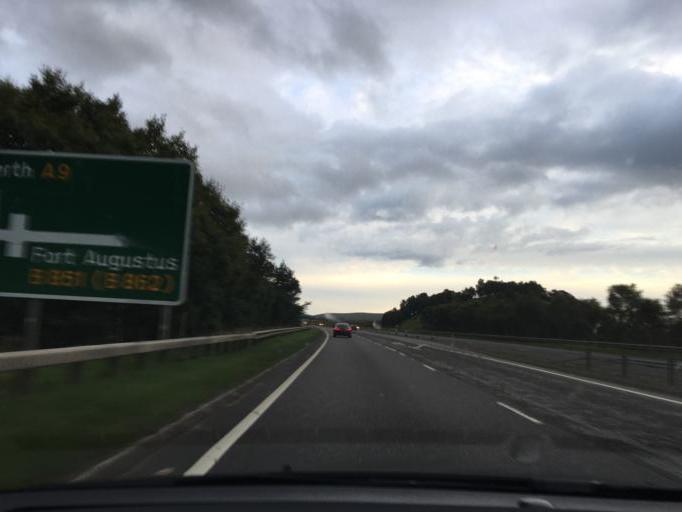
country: GB
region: Scotland
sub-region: Highland
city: Inverness
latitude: 57.4135
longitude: -4.1356
